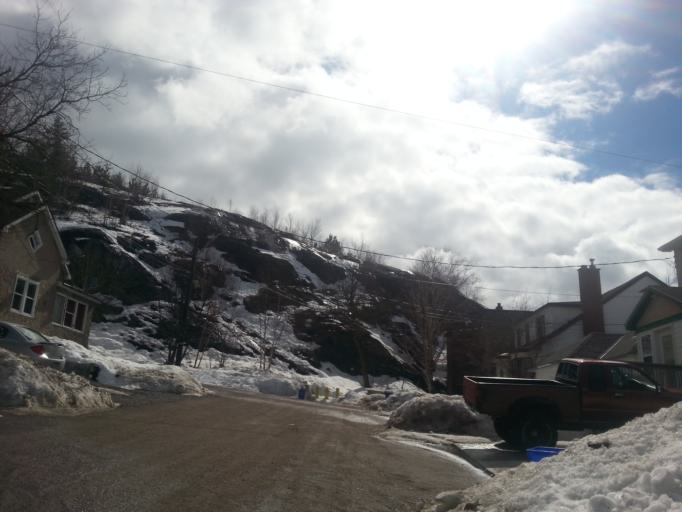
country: CA
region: Ontario
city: Greater Sudbury
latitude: 46.5019
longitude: -80.9969
